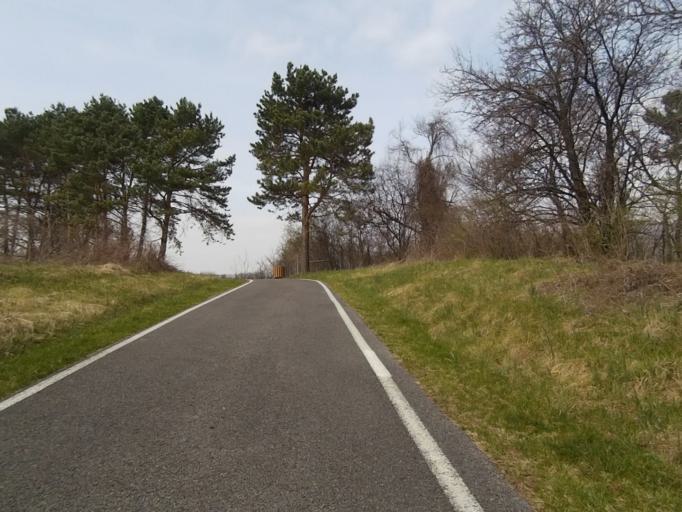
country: US
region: Pennsylvania
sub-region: Centre County
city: Lemont
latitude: 40.7915
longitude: -77.8154
